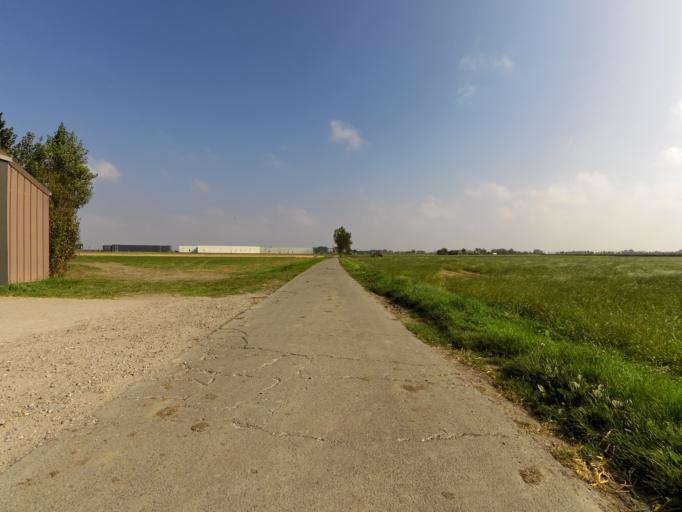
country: BE
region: Flanders
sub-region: Provincie West-Vlaanderen
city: Ostend
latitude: 51.1911
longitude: 2.8917
